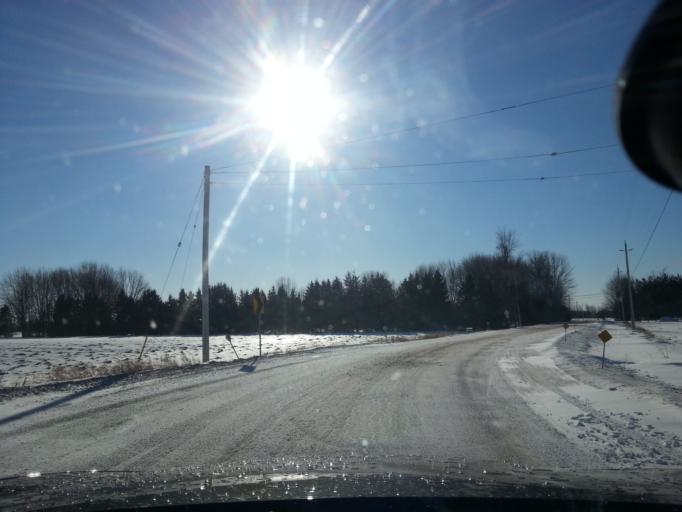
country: CA
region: Ontario
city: Clarence-Rockland
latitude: 45.2946
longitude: -75.4082
